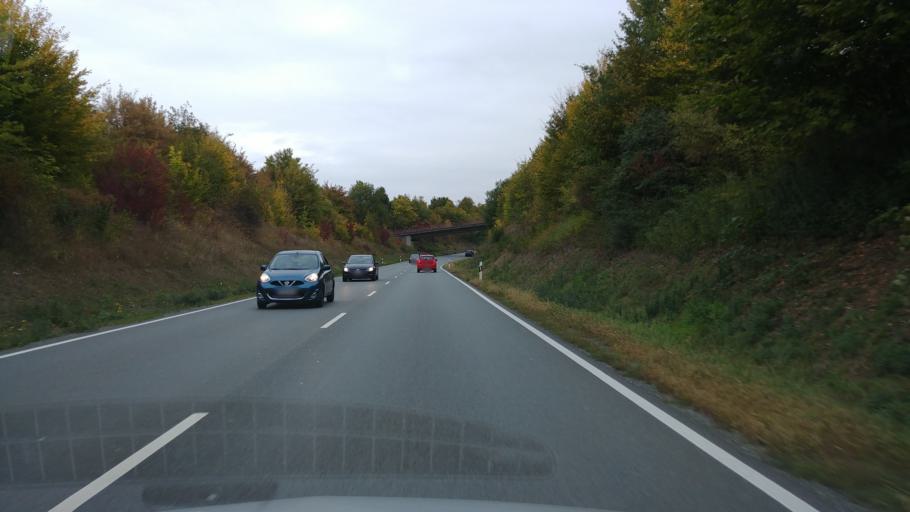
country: DE
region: Rheinland-Pfalz
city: Holzheim
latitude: 50.3657
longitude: 8.0331
